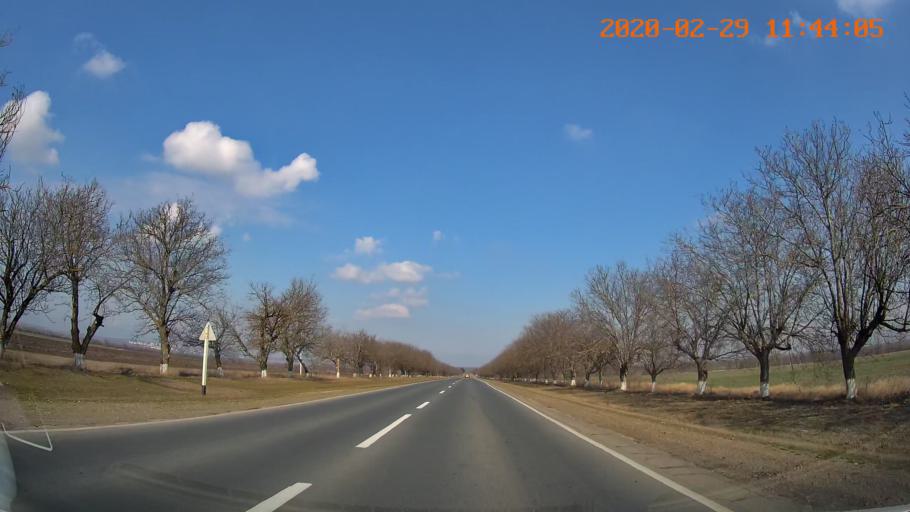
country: MD
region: Rezina
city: Saharna
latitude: 47.7060
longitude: 29.0010
